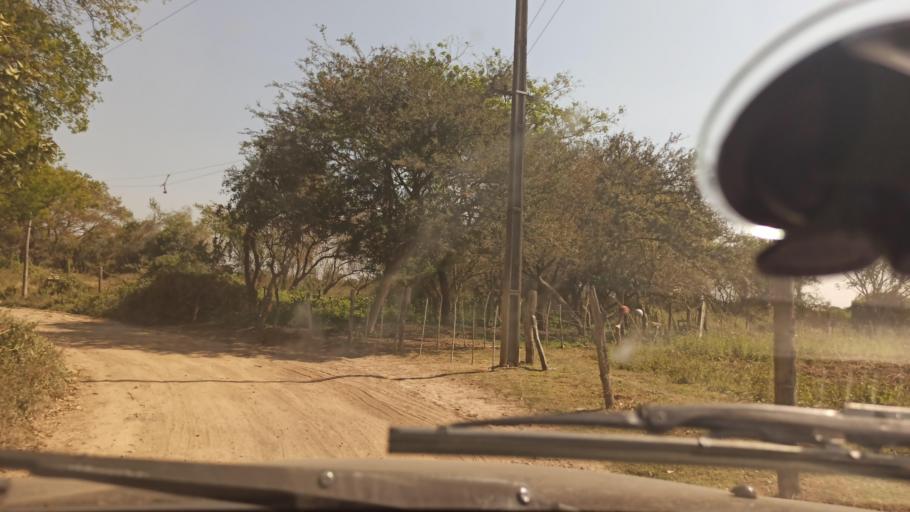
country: AR
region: Formosa
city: Clorinda
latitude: -25.3286
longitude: -57.6871
